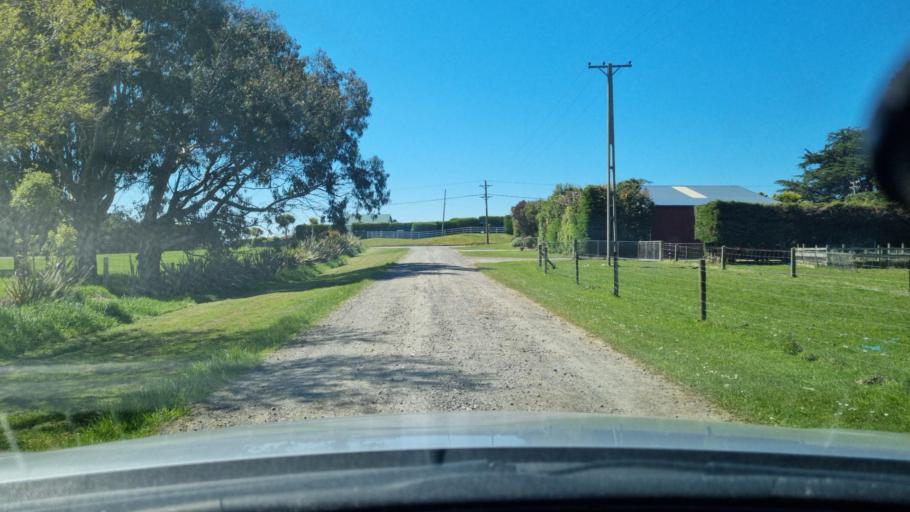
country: NZ
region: Southland
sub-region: Invercargill City
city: Invercargill
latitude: -46.4416
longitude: 168.2916
